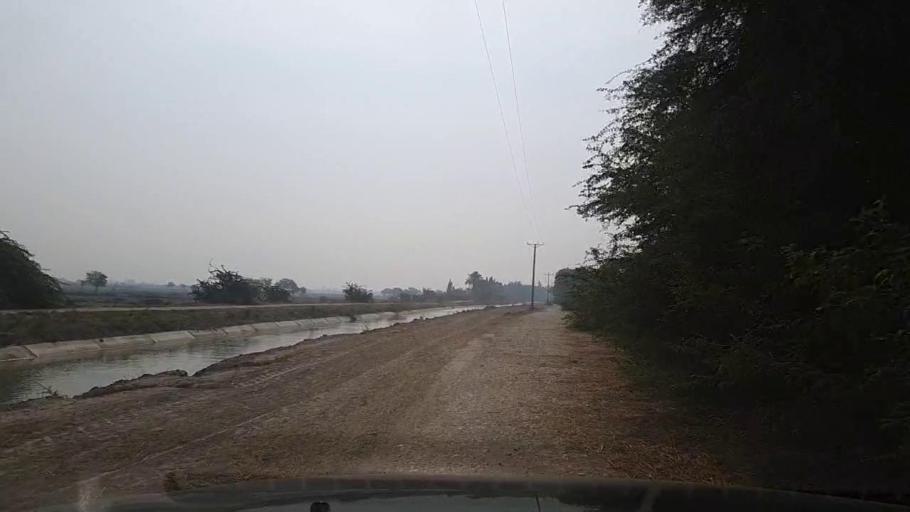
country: PK
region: Sindh
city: Mirpur Sakro
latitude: 24.5403
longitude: 67.8122
